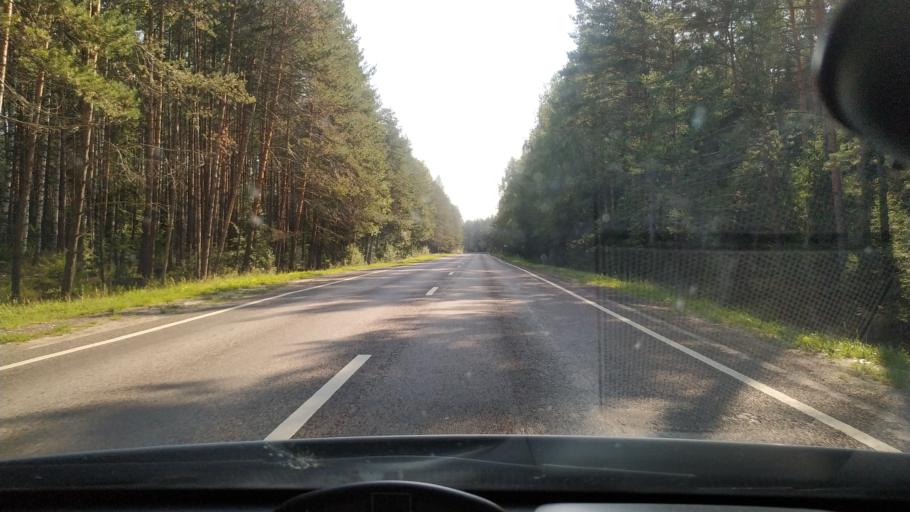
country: RU
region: Moskovskaya
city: Dmitrovskiy Pogost
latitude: 55.2358
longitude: 39.9669
